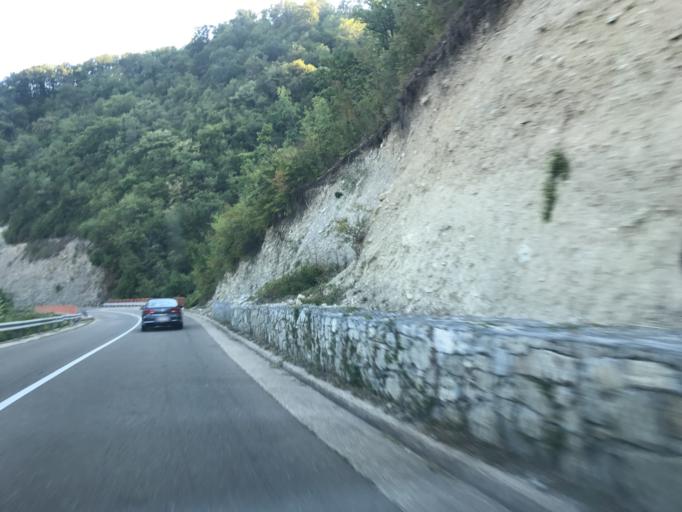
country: RO
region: Mehedinti
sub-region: Comuna Svinita
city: Svinita
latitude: 44.5535
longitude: 22.0267
